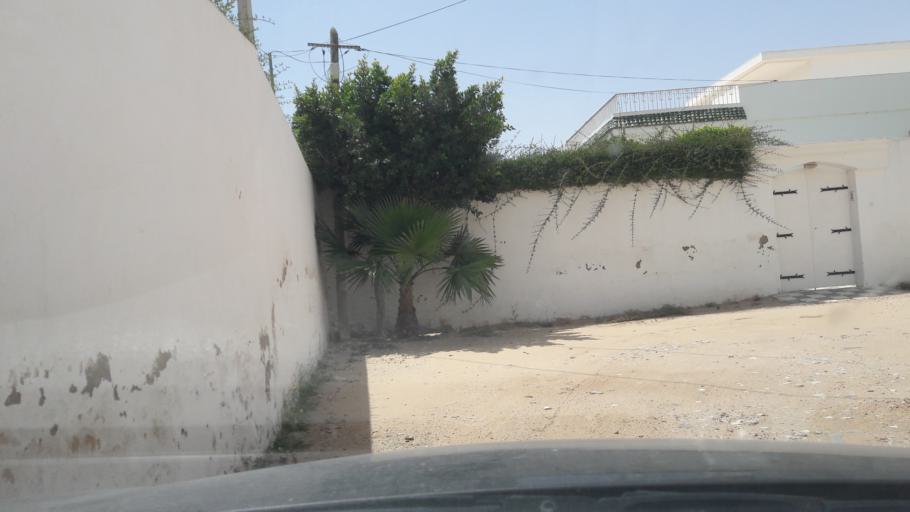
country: TN
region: Safaqis
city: Al Qarmadah
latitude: 34.7820
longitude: 10.7599
